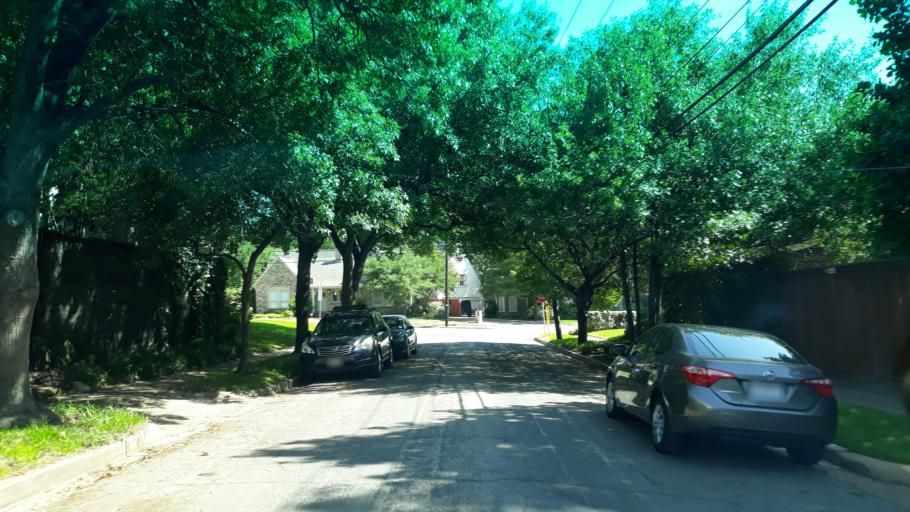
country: US
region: Texas
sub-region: Dallas County
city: Highland Park
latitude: 32.8133
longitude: -96.7589
